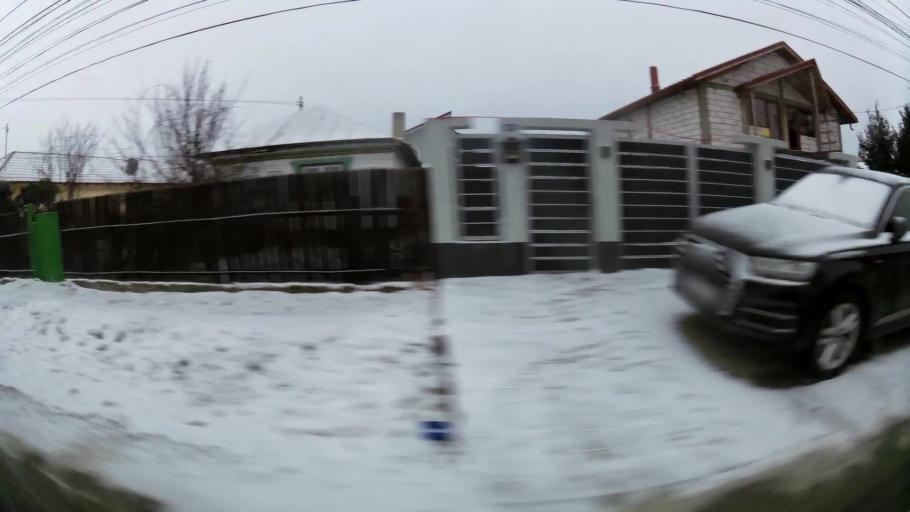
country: RO
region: Prahova
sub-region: Comuna Berceni
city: Corlatesti
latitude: 44.9164
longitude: 26.0828
